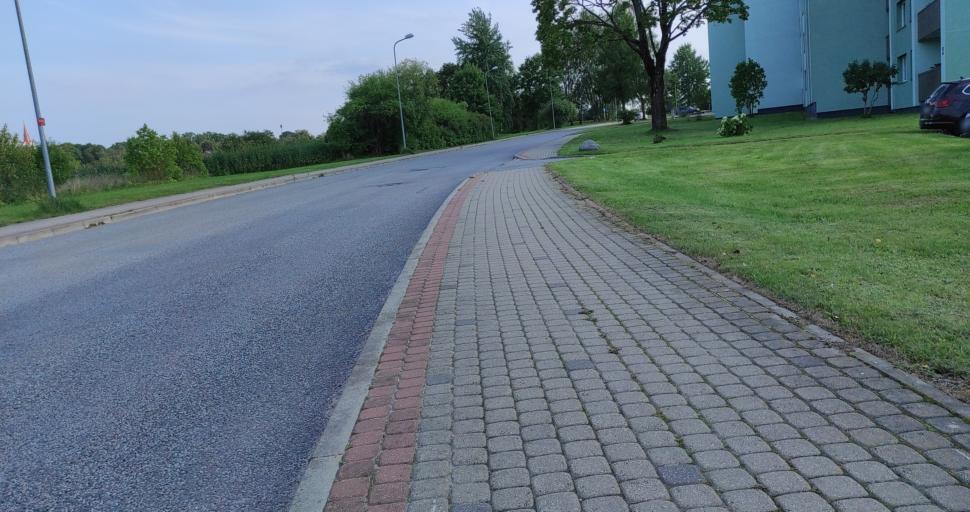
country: LV
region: Cesu Rajons
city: Cesis
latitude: 57.3174
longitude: 25.2592
